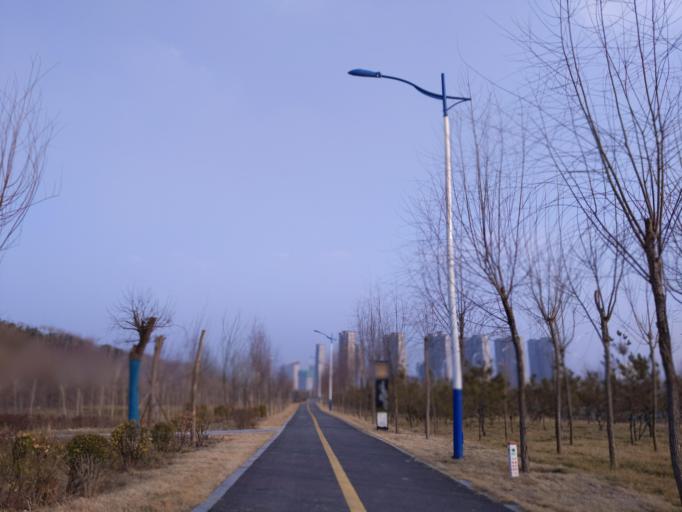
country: CN
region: Henan Sheng
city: Puyang
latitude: 35.8193
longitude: 115.0006
